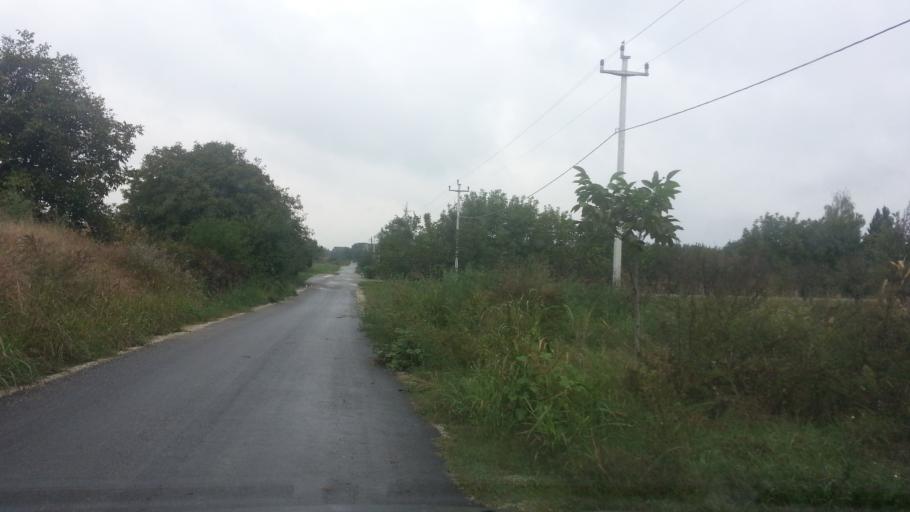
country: RS
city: Novi Banovci
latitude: 44.9385
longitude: 20.2958
